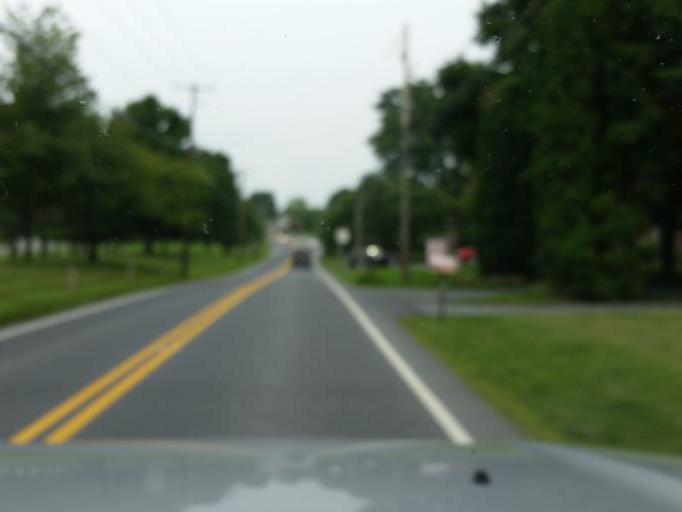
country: US
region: Pennsylvania
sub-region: Lancaster County
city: Lititz
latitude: 40.1537
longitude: -76.3195
